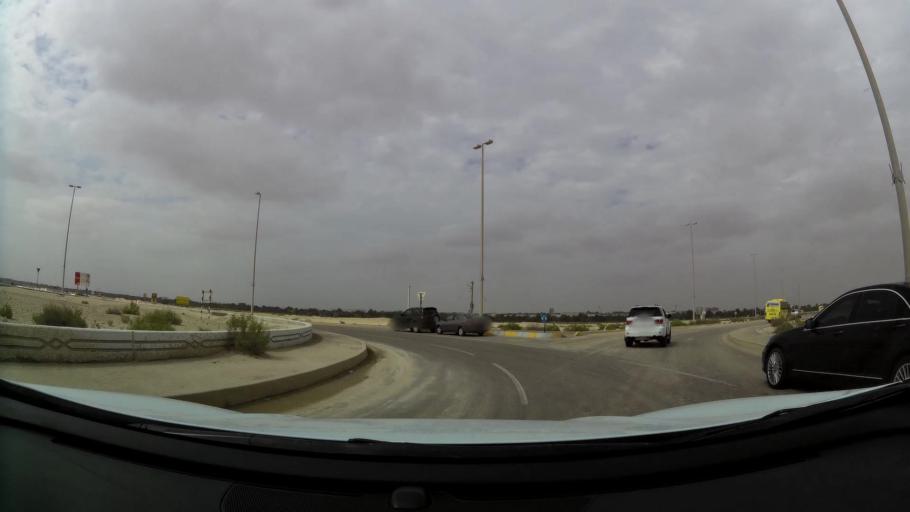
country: AE
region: Abu Dhabi
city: Abu Dhabi
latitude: 24.4031
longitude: 54.6525
